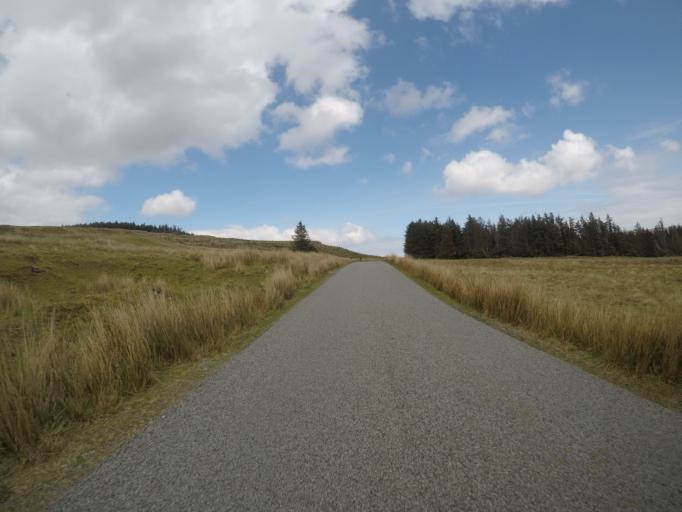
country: GB
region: Scotland
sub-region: Highland
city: Isle of Skye
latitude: 57.4063
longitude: -6.3244
